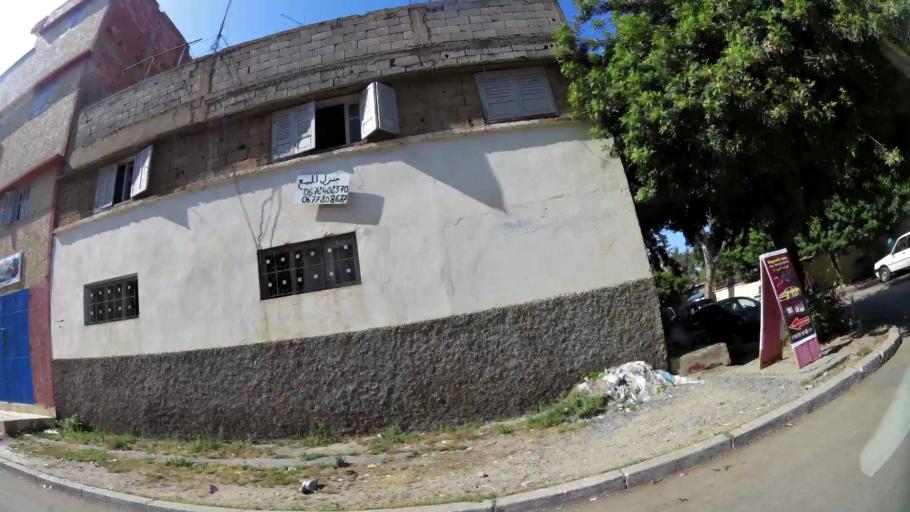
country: MA
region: Rabat-Sale-Zemmour-Zaer
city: Sale
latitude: 34.0460
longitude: -6.7824
